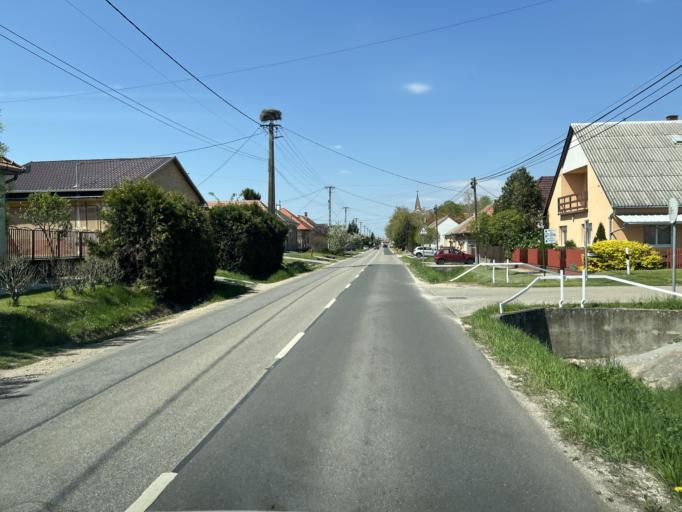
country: HU
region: Pest
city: Kakucs
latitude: 47.2398
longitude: 19.3685
